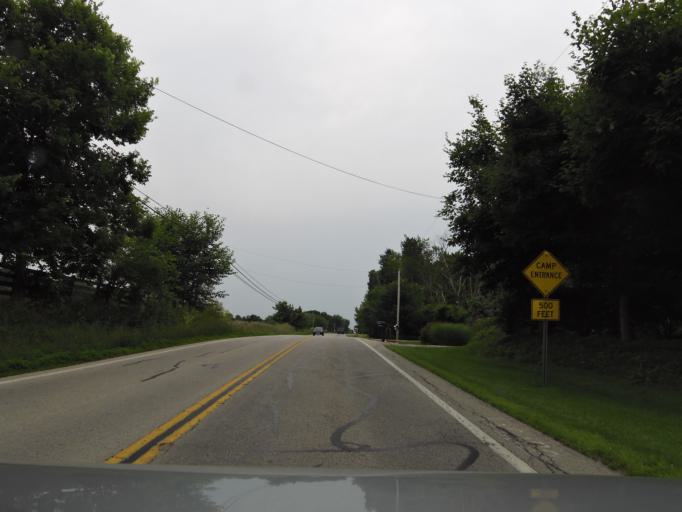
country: US
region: Ohio
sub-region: Clinton County
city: Wilmington
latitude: 39.4828
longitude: -83.9188
